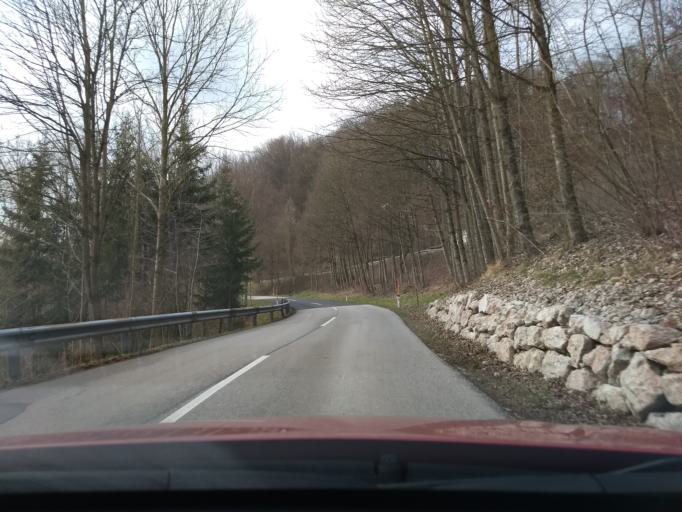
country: AT
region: Upper Austria
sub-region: Politischer Bezirk Steyr-Land
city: Garsten
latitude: 48.0015
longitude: 14.3990
